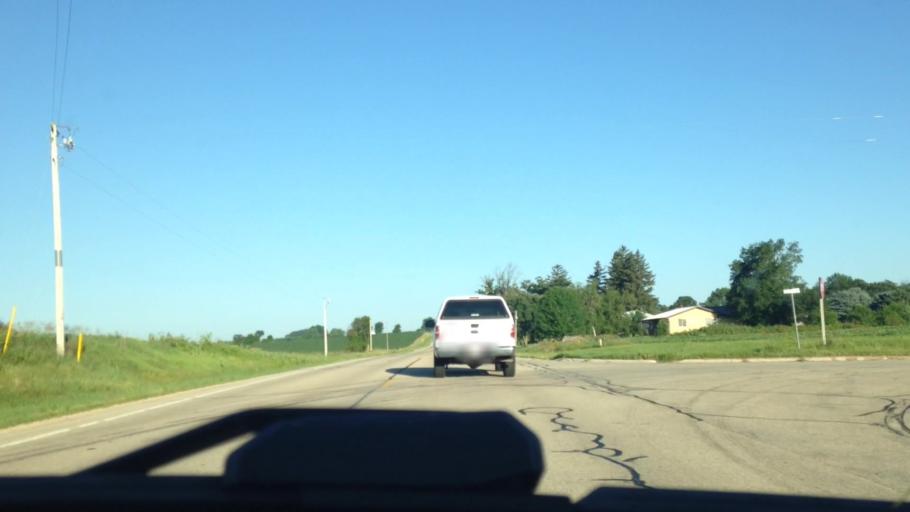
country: US
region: Wisconsin
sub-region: Columbia County
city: Rio
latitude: 43.3405
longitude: -89.1815
